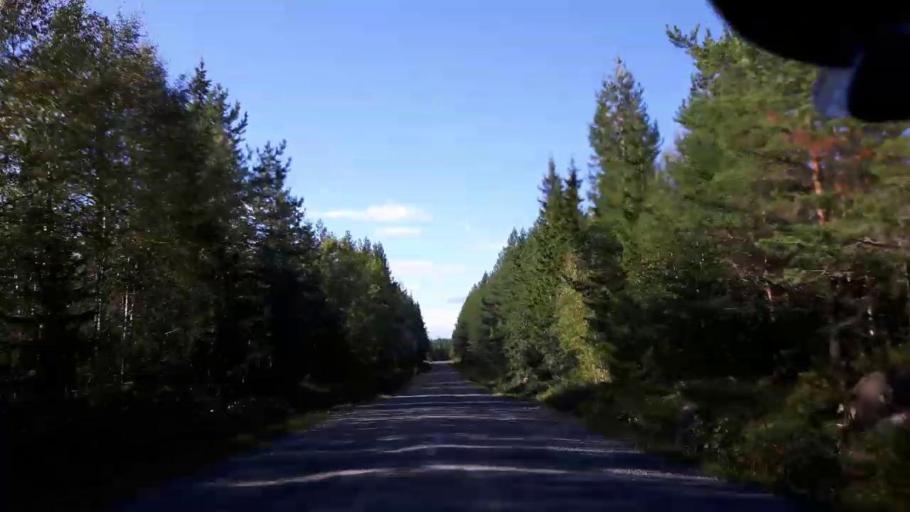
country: SE
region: Jaemtland
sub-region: Ragunda Kommun
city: Hammarstrand
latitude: 63.5320
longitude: 16.0758
